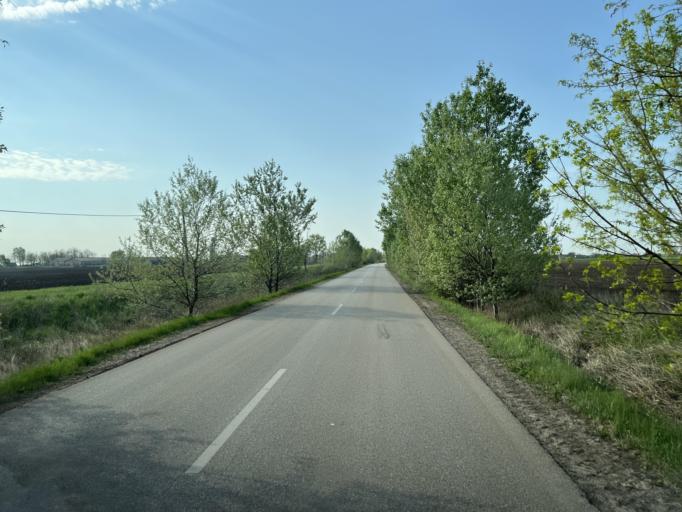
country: HU
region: Pest
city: Jaszkarajeno
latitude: 47.1081
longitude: 20.0177
